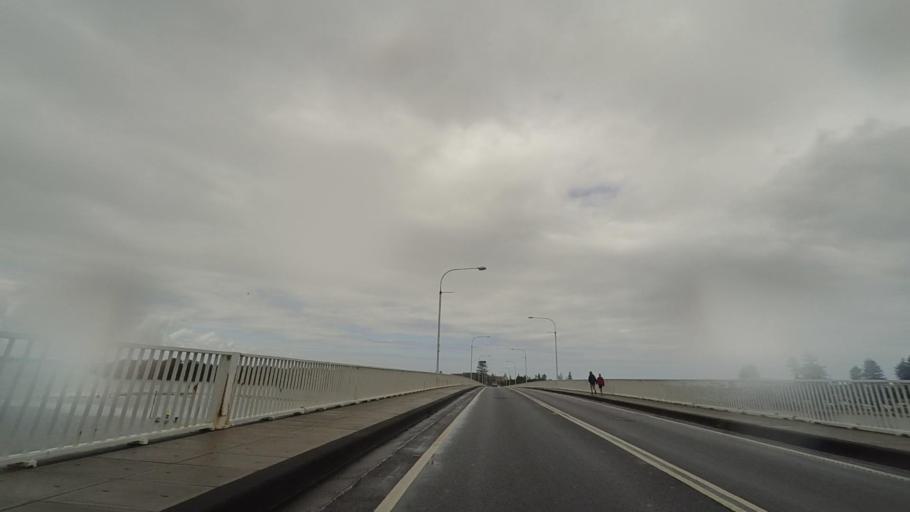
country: AU
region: New South Wales
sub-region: Wyong Shire
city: The Entrance
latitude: -33.3385
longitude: 151.4990
